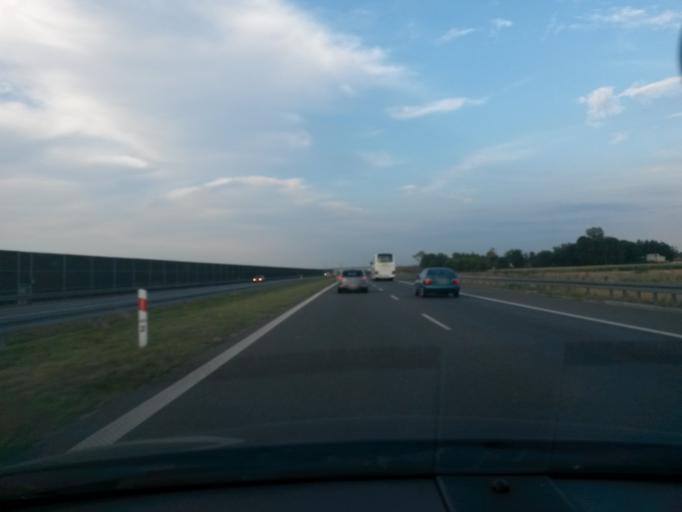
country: PL
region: Masovian Voivodeship
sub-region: Powiat warszawski zachodni
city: Bieniewice
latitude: 52.1299
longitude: 20.5436
